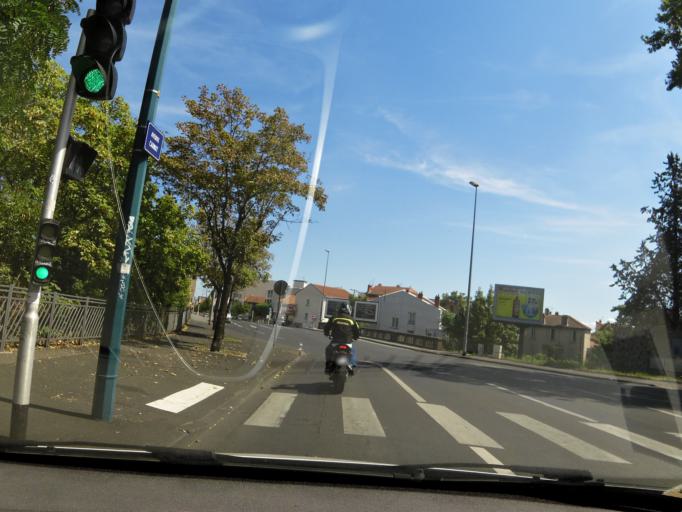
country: FR
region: Auvergne
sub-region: Departement du Puy-de-Dome
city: Clermont-Ferrand
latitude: 45.7762
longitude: 3.0977
